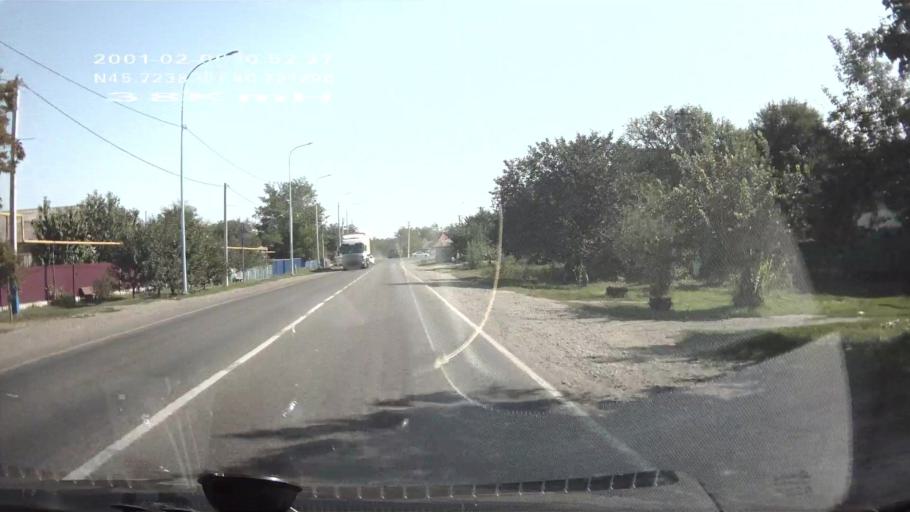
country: RU
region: Krasnodarskiy
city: Dmitriyevskaya
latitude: 45.7235
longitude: 40.7218
